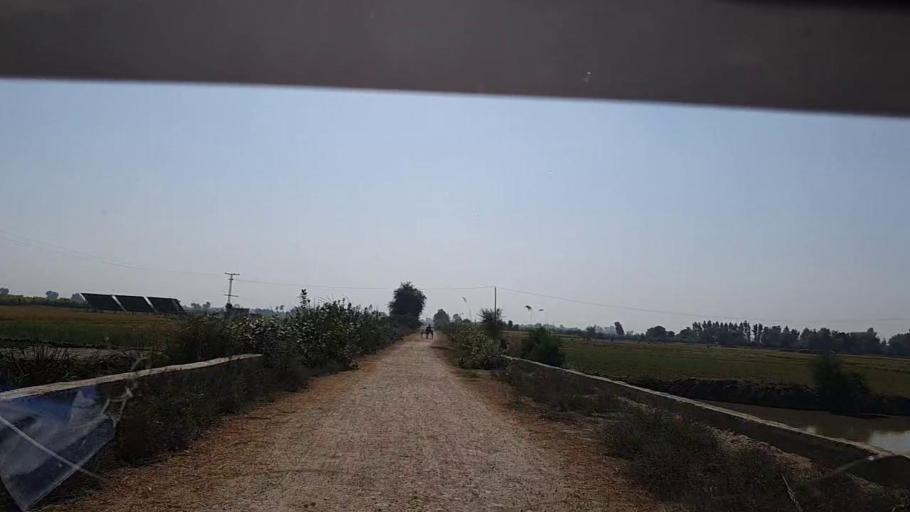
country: PK
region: Sindh
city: Naudero
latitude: 27.6970
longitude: 68.4021
